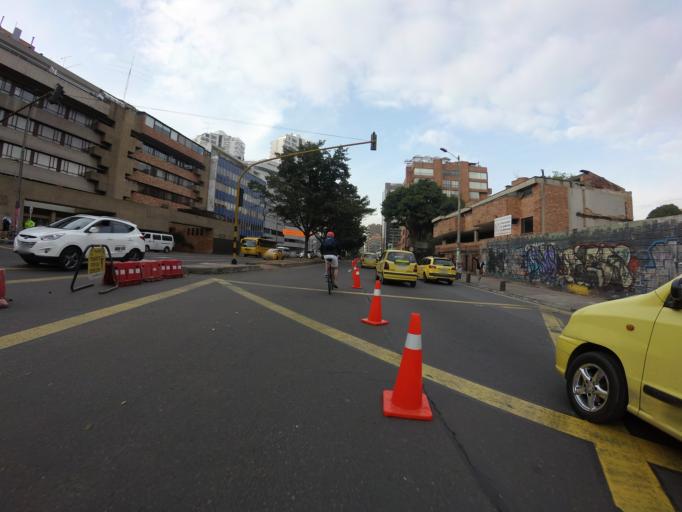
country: CO
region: Bogota D.C.
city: Barrio San Luis
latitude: 4.6641
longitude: -74.0477
